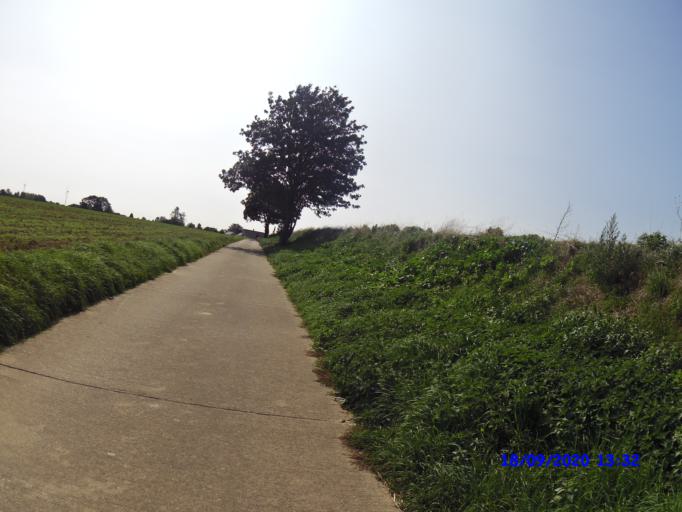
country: BE
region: Flanders
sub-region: Provincie Limburg
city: Gingelom
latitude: 50.7279
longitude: 5.1327
